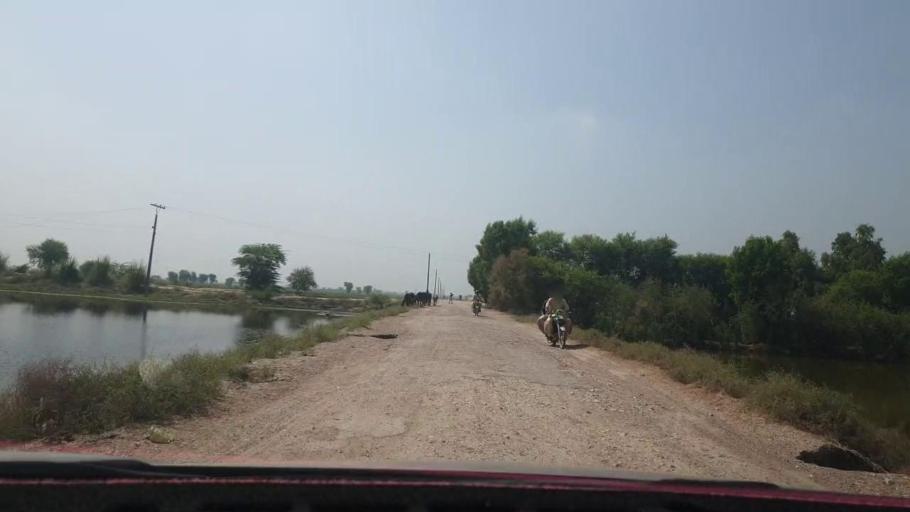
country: PK
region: Sindh
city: Warah
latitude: 27.4157
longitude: 67.8444
